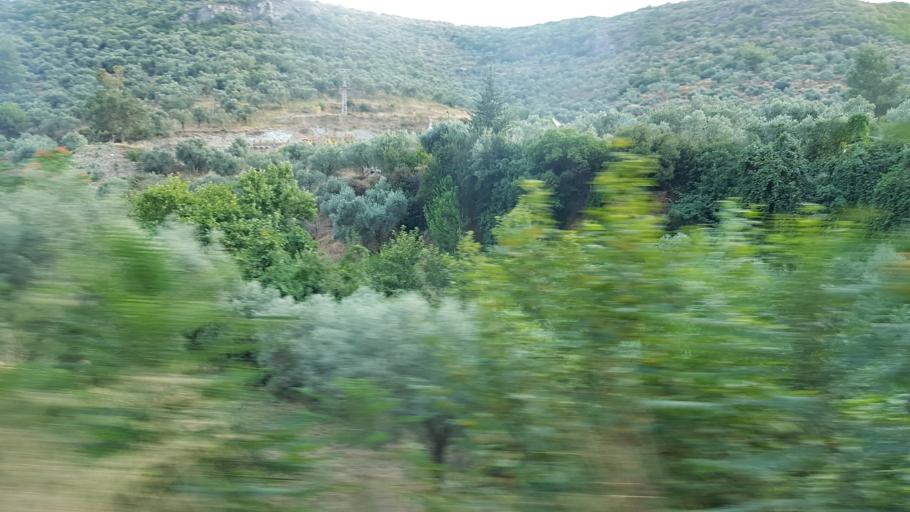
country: TR
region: Izmir
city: Selcuk
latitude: 37.9592
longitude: 27.4146
